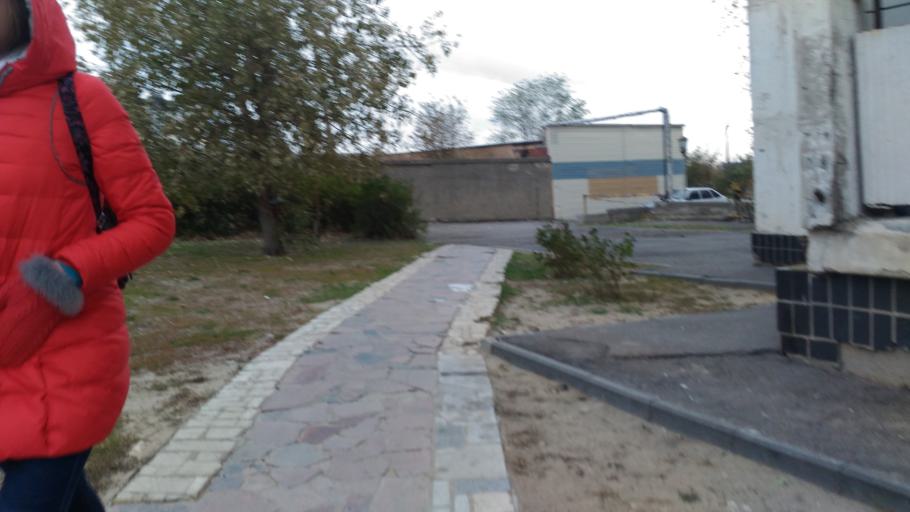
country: RU
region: Volgograd
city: Volgograd
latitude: 48.6420
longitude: 44.4299
